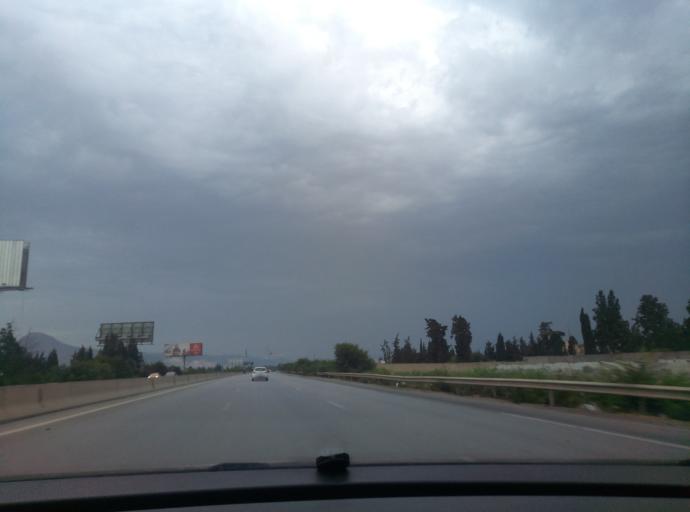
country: TN
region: Tunis
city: Rades
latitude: 36.7227
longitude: 10.2600
